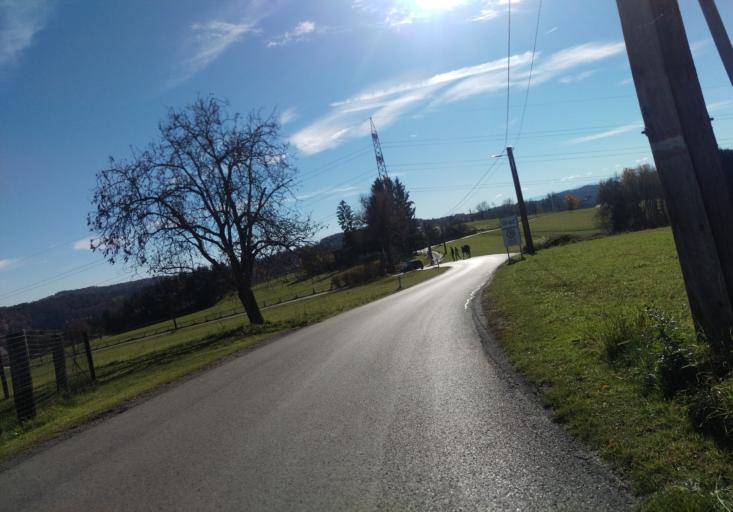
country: AT
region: Styria
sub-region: Graz Stadt
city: Mariatrost
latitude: 47.1183
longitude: 15.4949
